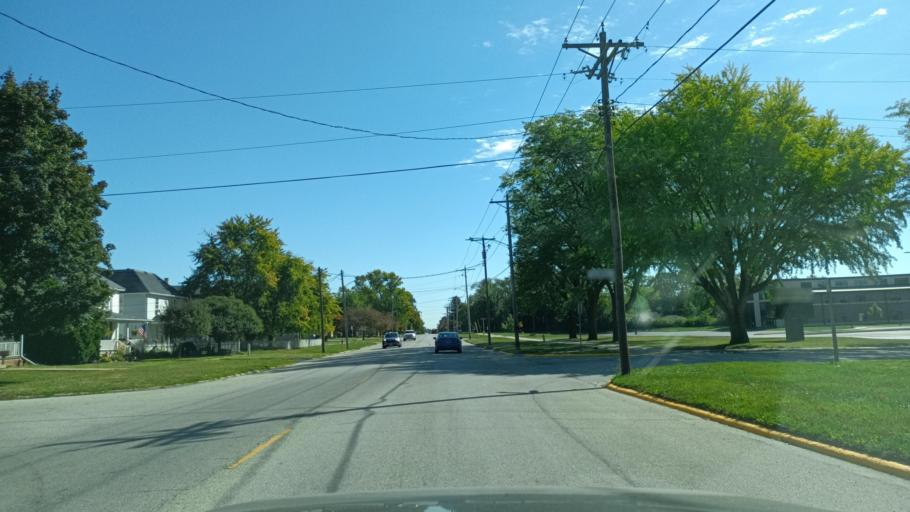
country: US
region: Illinois
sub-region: Knox County
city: Knoxville
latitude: 40.9079
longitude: -90.2769
